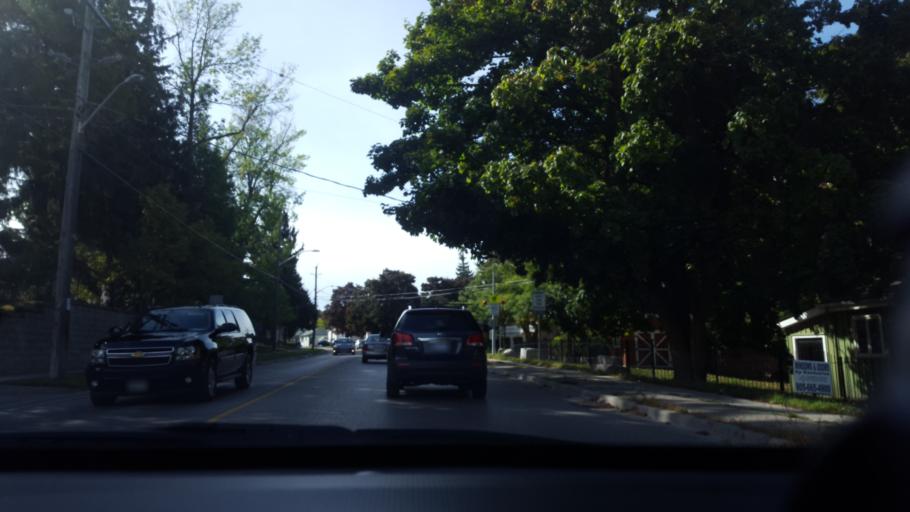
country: CA
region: Ontario
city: Newmarket
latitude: 44.0487
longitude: -79.4531
